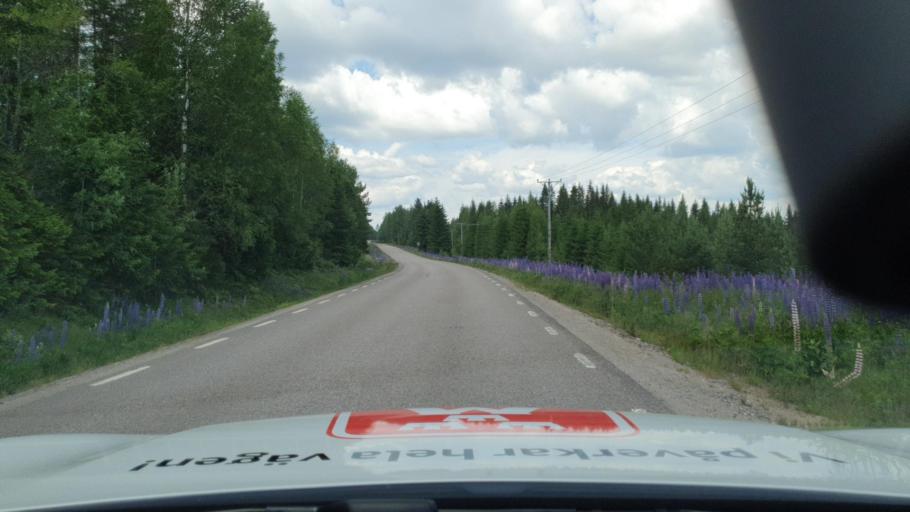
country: SE
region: Vaermland
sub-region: Torsby Kommun
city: Torsby
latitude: 60.4787
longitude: 12.8808
